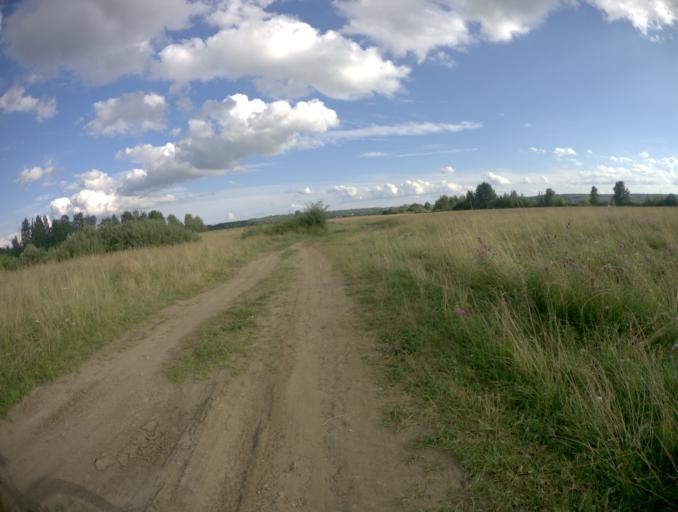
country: RU
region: Vladimir
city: Raduzhnyy
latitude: 56.0390
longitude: 40.3093
